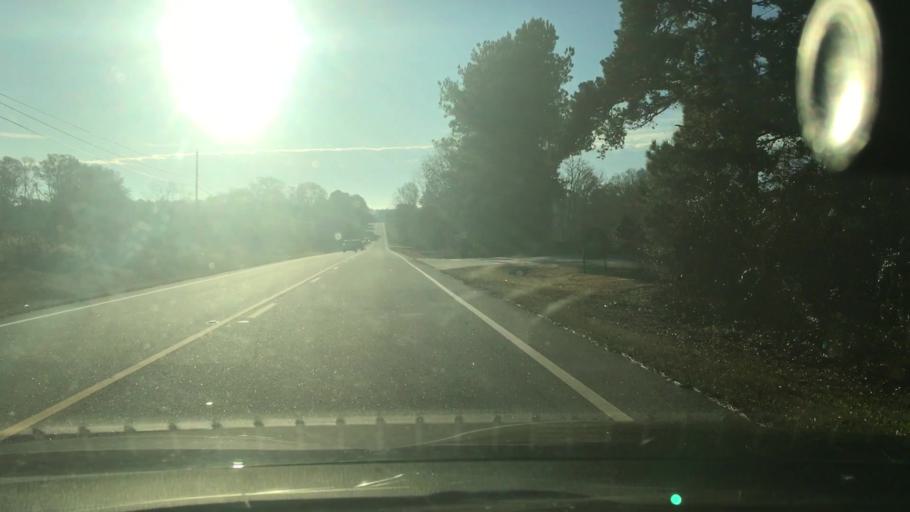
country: US
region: Georgia
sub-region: Coweta County
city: Senoia
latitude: 33.2719
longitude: -84.5283
